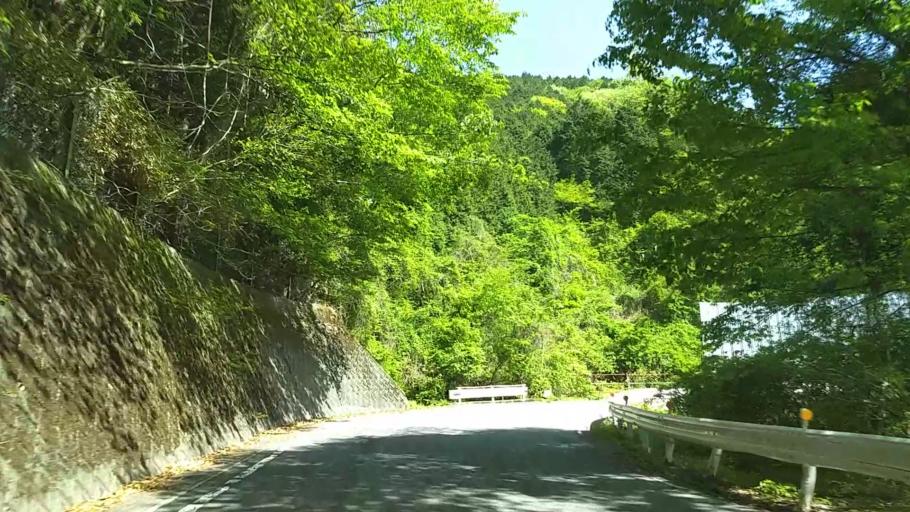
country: JP
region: Shizuoka
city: Gotemba
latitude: 35.2743
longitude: 138.9640
